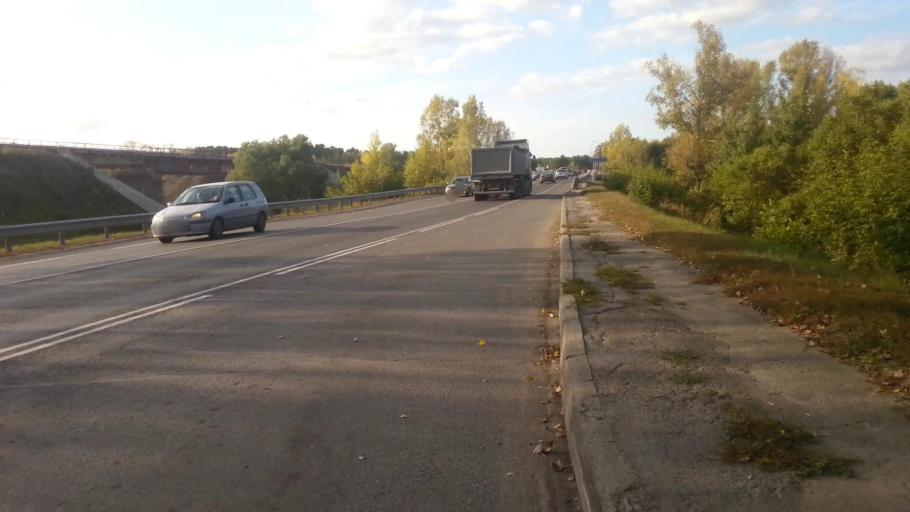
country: RU
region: Altai Krai
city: Yuzhnyy
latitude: 53.3052
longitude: 83.7036
